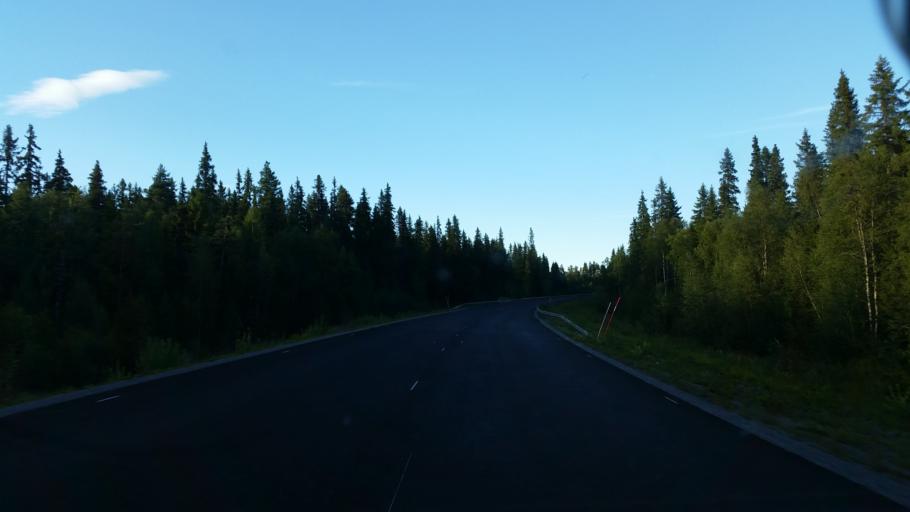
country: SE
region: Vaesterbotten
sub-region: Dorotea Kommun
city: Dorotea
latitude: 64.2836
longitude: 16.5052
